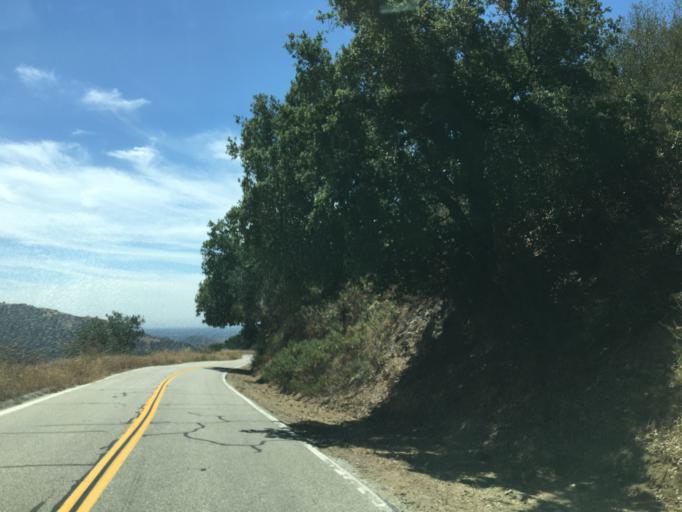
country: US
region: California
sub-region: Los Angeles County
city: Glendora
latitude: 34.1731
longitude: -117.8497
